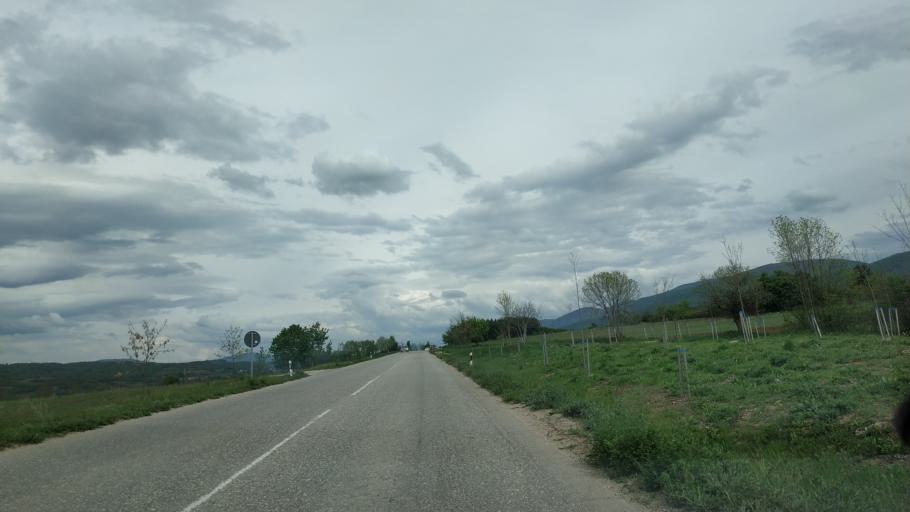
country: RS
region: Central Serbia
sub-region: Zajecarski Okrug
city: Soko Banja
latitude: 43.6555
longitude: 21.8294
